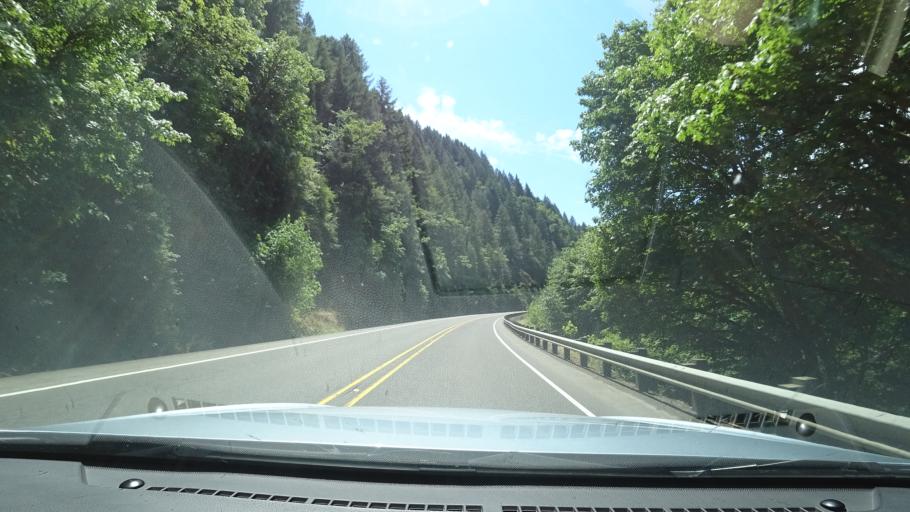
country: US
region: Oregon
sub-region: Lane County
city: Veneta
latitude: 43.9992
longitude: -123.6704
